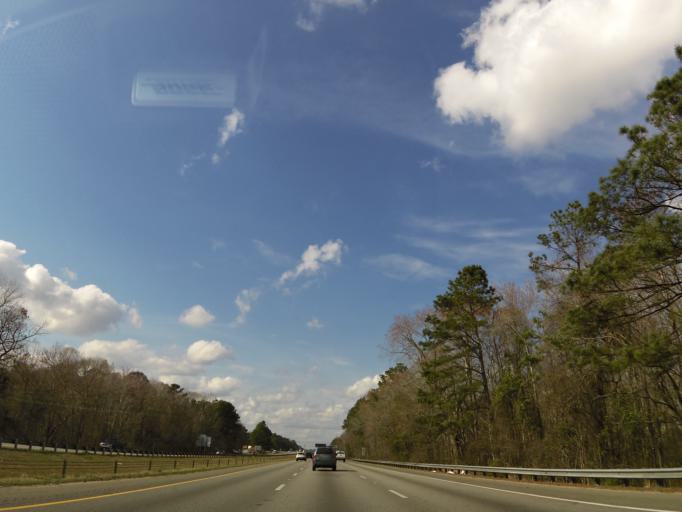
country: US
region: South Carolina
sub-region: Berkeley County
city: Ladson
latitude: 32.9863
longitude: -80.0807
